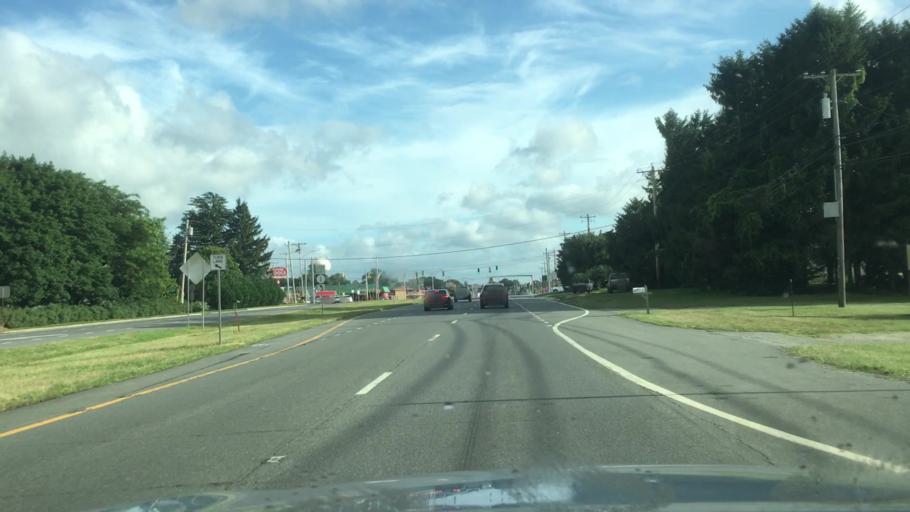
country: US
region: Delaware
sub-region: Sussex County
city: Milford
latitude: 38.9349
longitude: -75.4298
